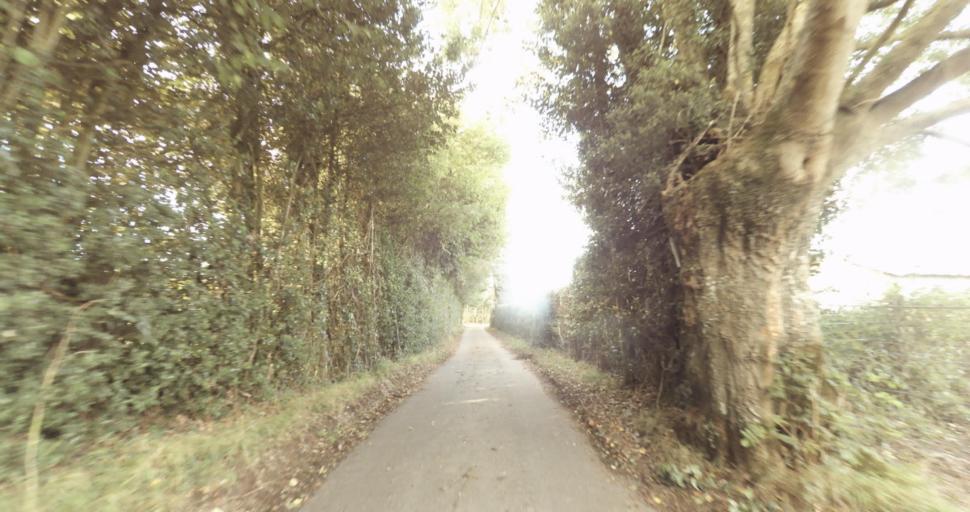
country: FR
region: Lower Normandy
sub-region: Departement de l'Orne
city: Vimoutiers
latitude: 48.8872
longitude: 0.2295
